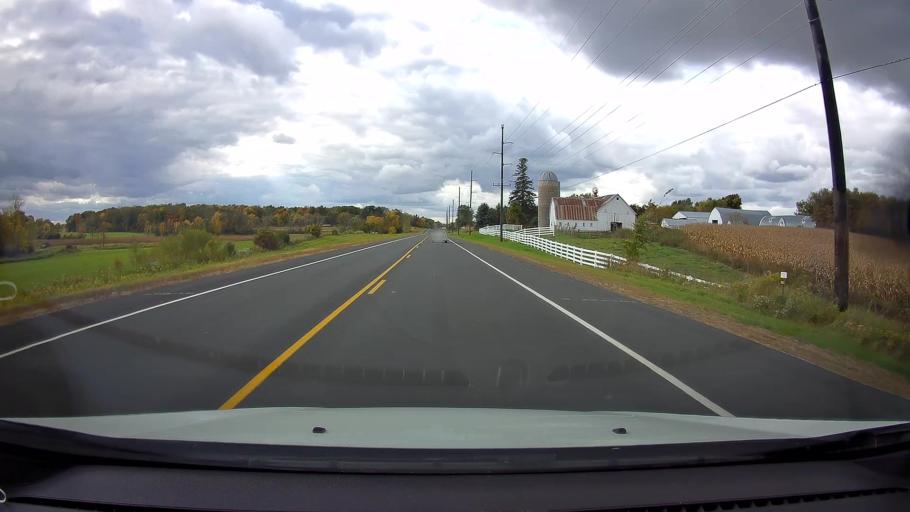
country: US
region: Minnesota
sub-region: Chisago County
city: Center City
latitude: 45.3972
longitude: -92.7849
